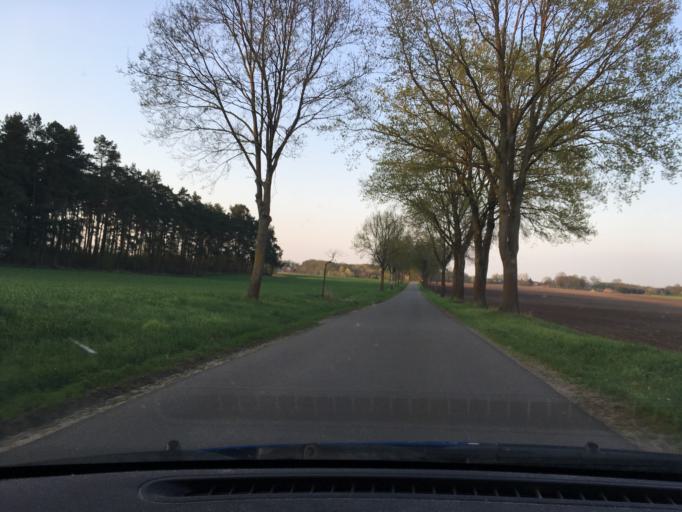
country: DE
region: Lower Saxony
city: Sudergellersen
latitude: 53.1974
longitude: 10.2827
